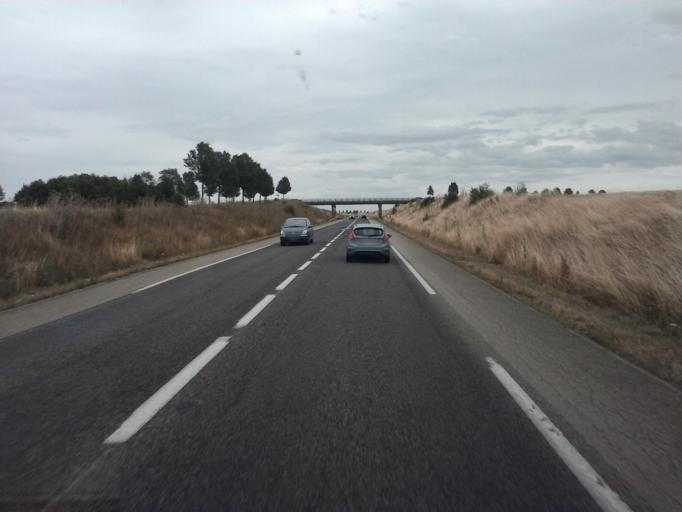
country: FR
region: Lorraine
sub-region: Departement de Meurthe-et-Moselle
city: Bainville-sur-Madon
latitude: 48.5773
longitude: 6.0717
